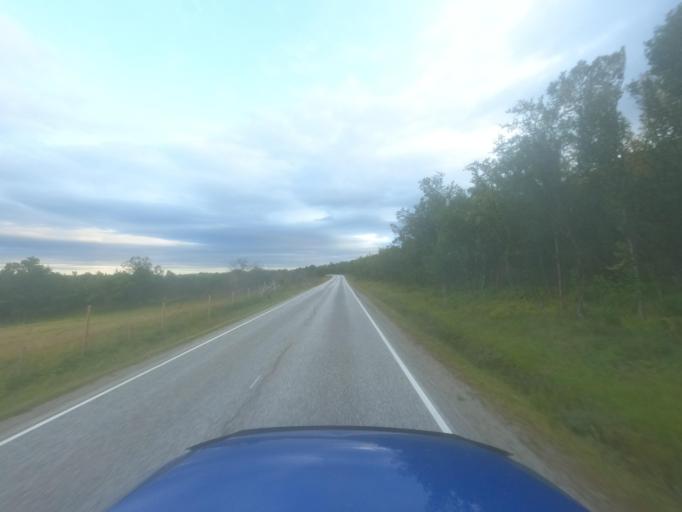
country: NO
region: Finnmark Fylke
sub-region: Porsanger
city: Lakselv
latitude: 70.4718
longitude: 25.2218
